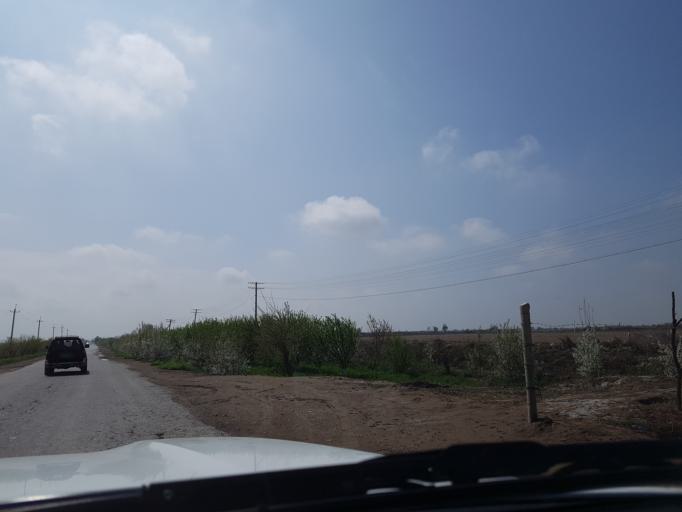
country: TM
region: Lebap
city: Turkmenabat
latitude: 38.9638
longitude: 63.6791
